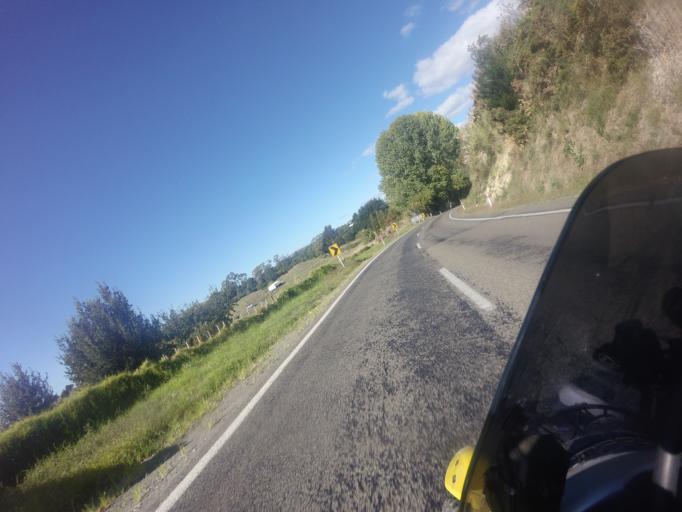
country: NZ
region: Bay of Plenty
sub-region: Whakatane District
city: Whakatane
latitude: -38.0190
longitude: 177.0948
